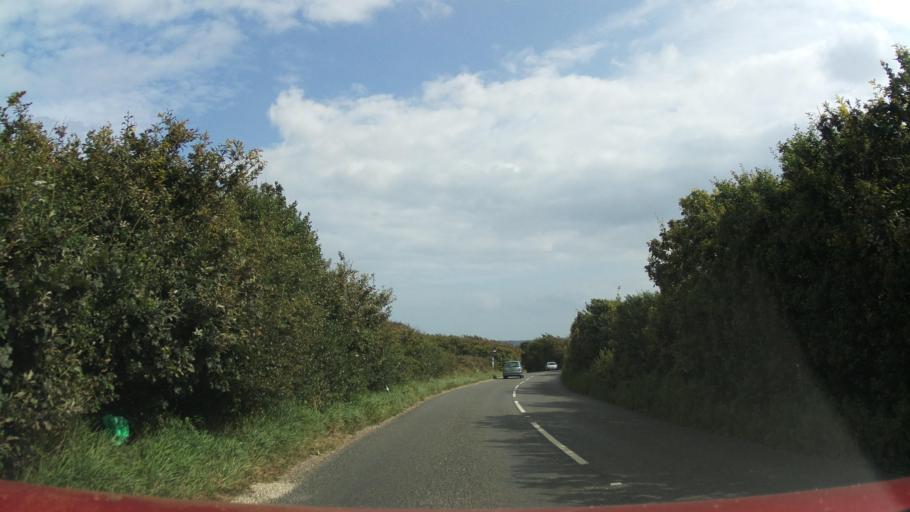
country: GB
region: England
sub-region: Hampshire
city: Milford on Sea
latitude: 50.7352
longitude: -1.6300
